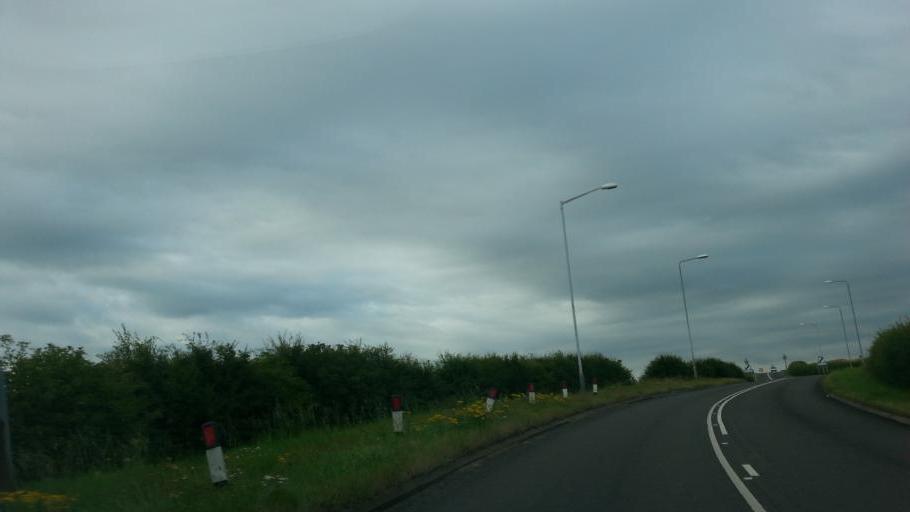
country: GB
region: England
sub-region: Nottinghamshire
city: Farndon
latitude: 53.0356
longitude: -0.8799
